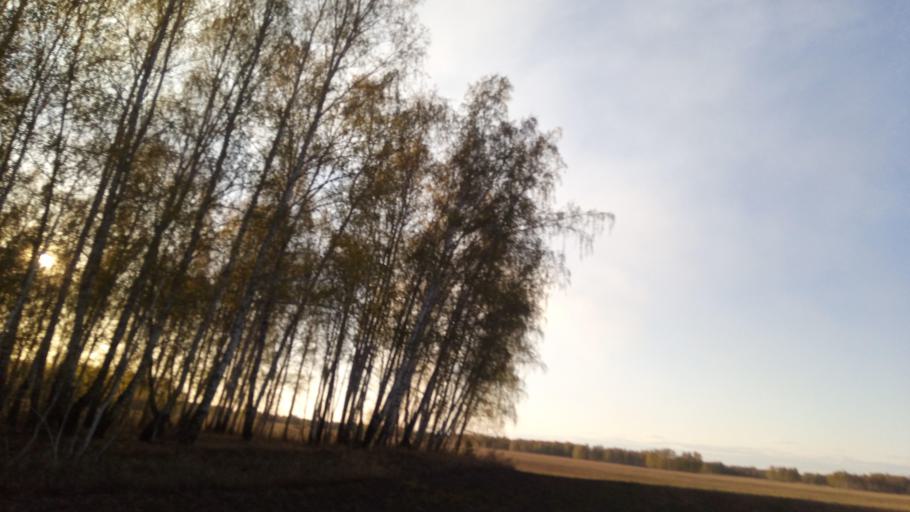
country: RU
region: Chelyabinsk
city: Timiryazevskiy
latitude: 54.9944
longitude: 60.8682
